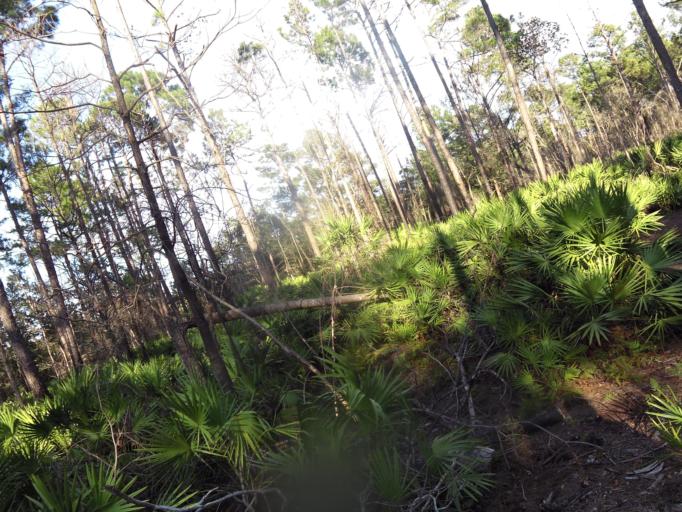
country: US
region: Florida
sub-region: Clay County
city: Bellair-Meadowbrook Terrace
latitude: 30.2443
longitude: -81.7038
